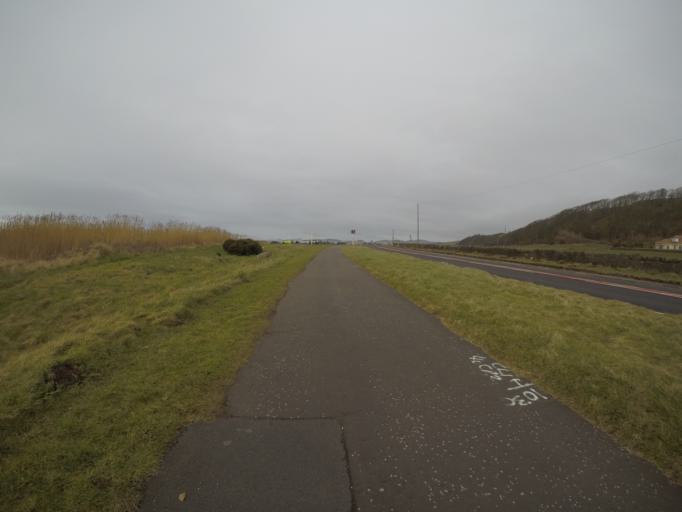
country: GB
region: Scotland
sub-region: North Ayrshire
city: West Kilbride
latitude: 55.6685
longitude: -4.8431
